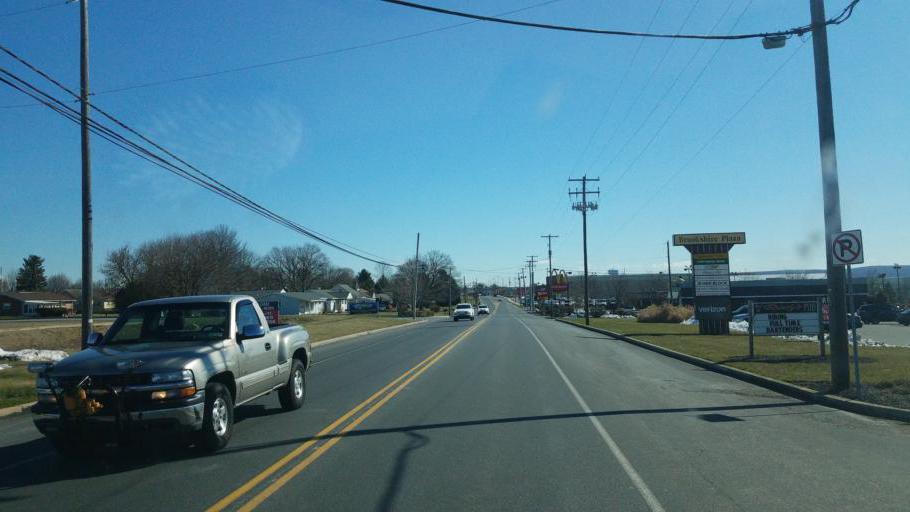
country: US
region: Pennsylvania
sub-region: Lancaster County
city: New Holland
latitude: 40.0927
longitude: -76.1185
